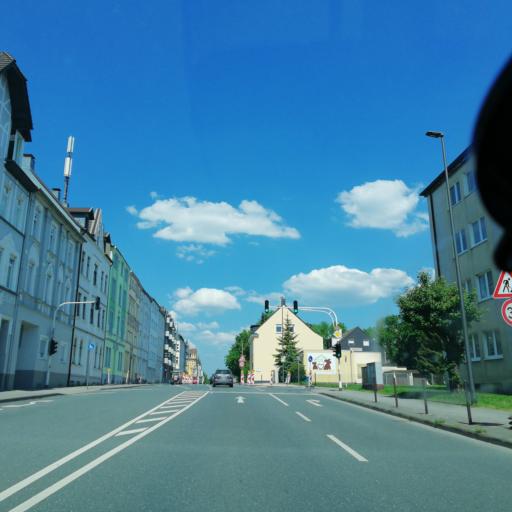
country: DE
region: North Rhine-Westphalia
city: Wulfrath
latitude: 51.2396
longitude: 7.0700
